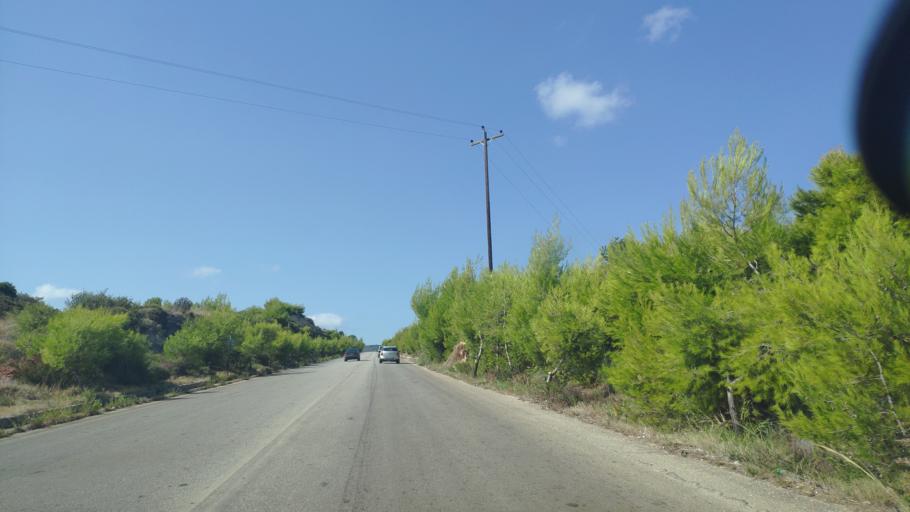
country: GR
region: Peloponnese
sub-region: Nomos Korinthias
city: Sikyon
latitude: 37.9891
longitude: 22.6906
